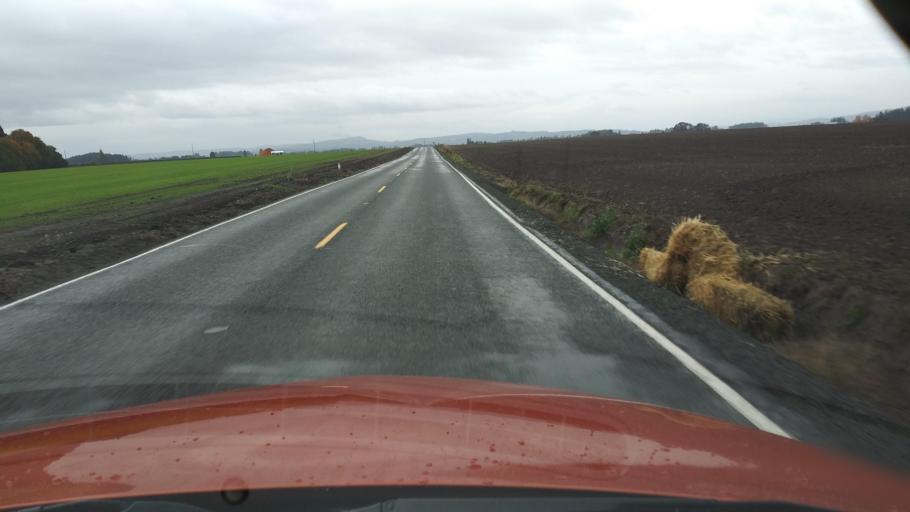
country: US
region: Oregon
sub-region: Washington County
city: North Plains
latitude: 45.5783
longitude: -123.0197
